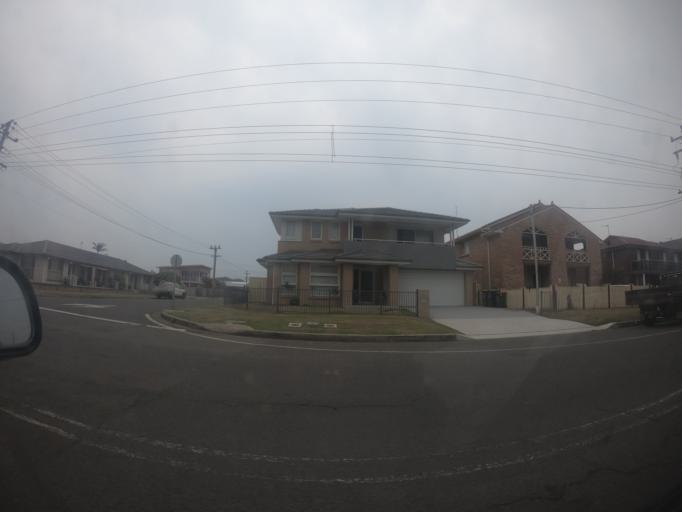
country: AU
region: New South Wales
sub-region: Shellharbour
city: Lake Illawarra
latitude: -34.5510
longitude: 150.8676
